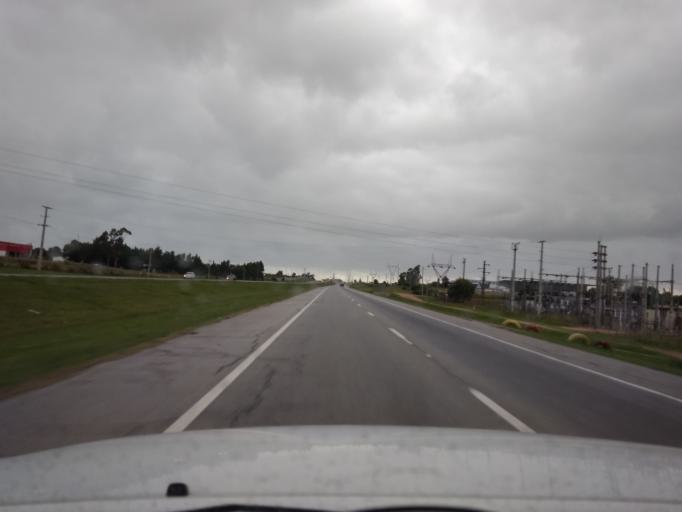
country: UY
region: Canelones
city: Las Piedras
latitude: -34.7117
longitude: -56.2431
